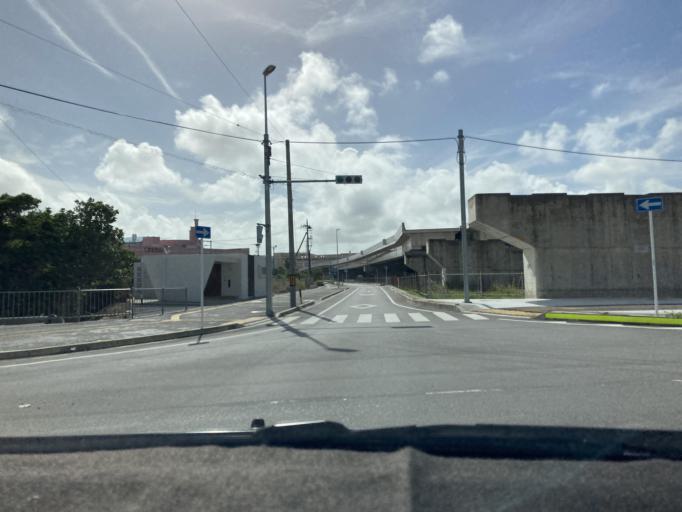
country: JP
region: Okinawa
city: Naha-shi
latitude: 26.2043
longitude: 127.7343
